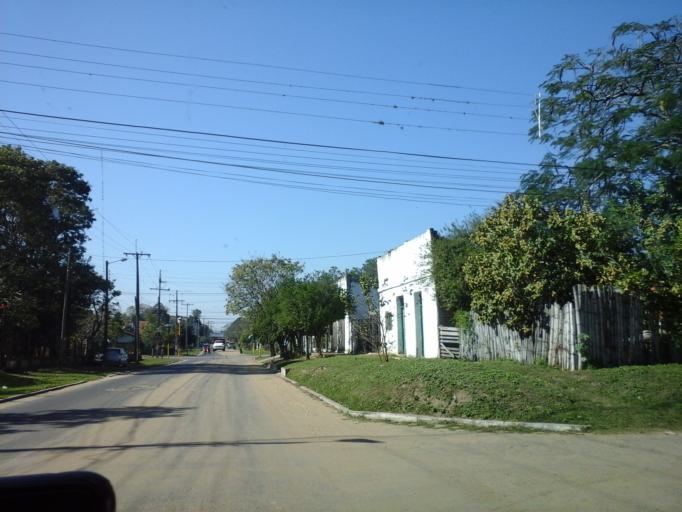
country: PY
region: Neembucu
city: Pilar
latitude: -26.8614
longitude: -58.3080
